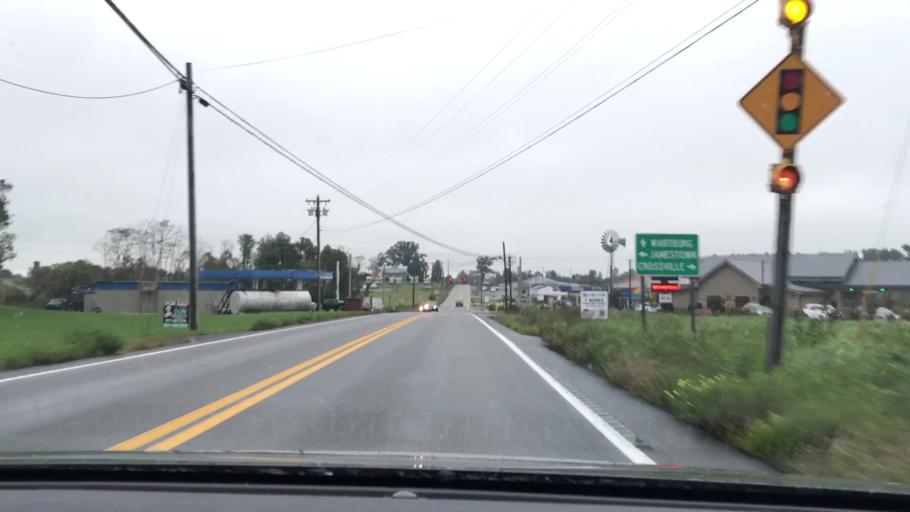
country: US
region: Tennessee
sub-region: Fentress County
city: Grimsley
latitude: 36.1853
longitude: -85.0217
